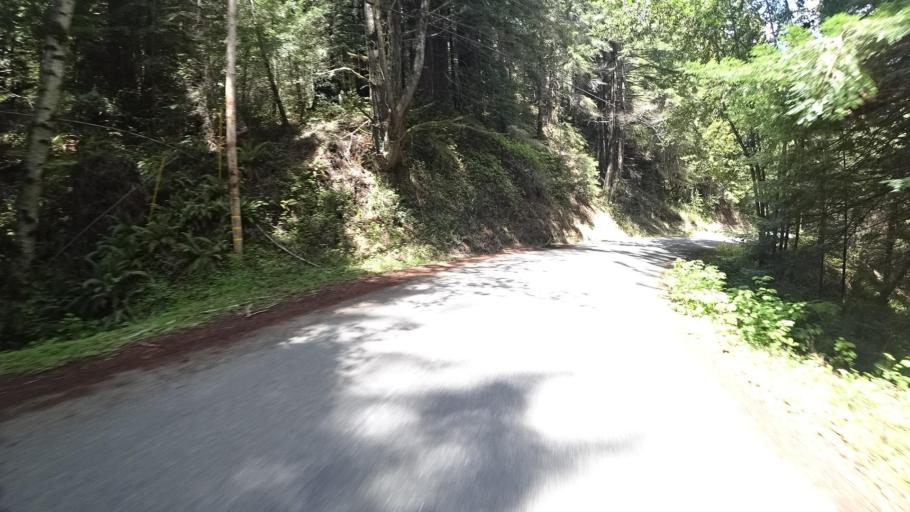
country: US
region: California
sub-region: Humboldt County
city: Blue Lake
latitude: 40.8442
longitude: -123.8986
